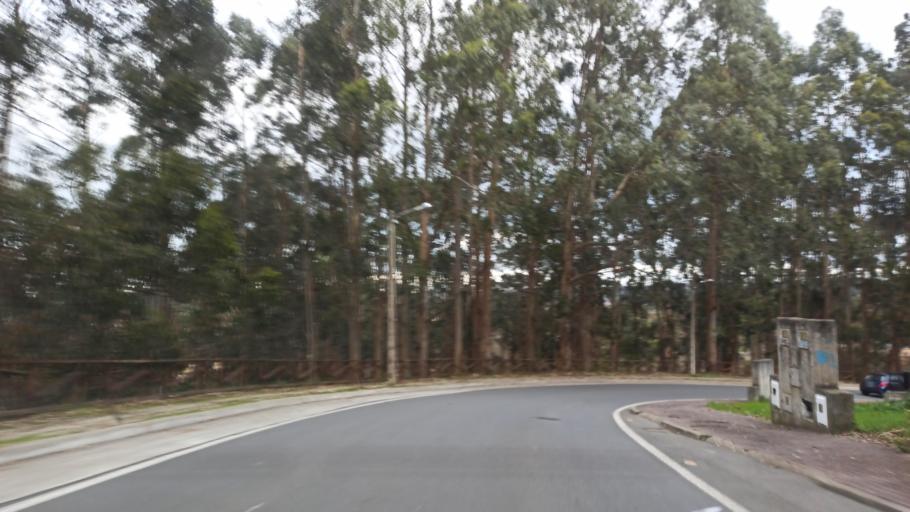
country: ES
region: Galicia
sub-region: Provincia da Coruna
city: Oleiros
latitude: 43.3346
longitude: -8.3540
